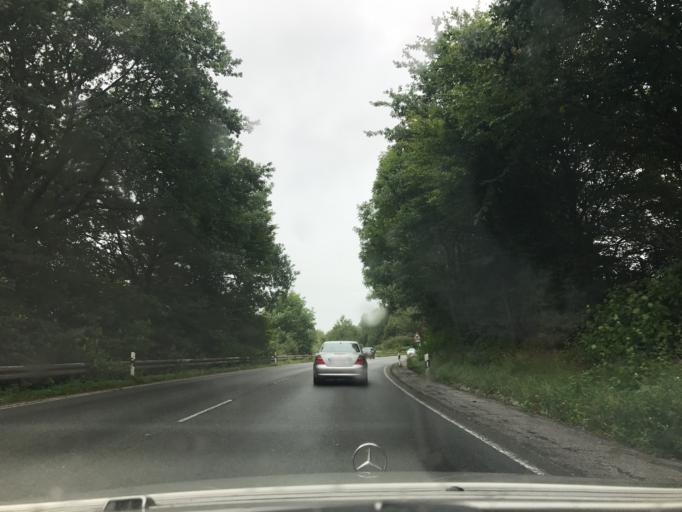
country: DE
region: North Rhine-Westphalia
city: Wetter (Ruhr)
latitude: 51.3545
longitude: 7.3915
